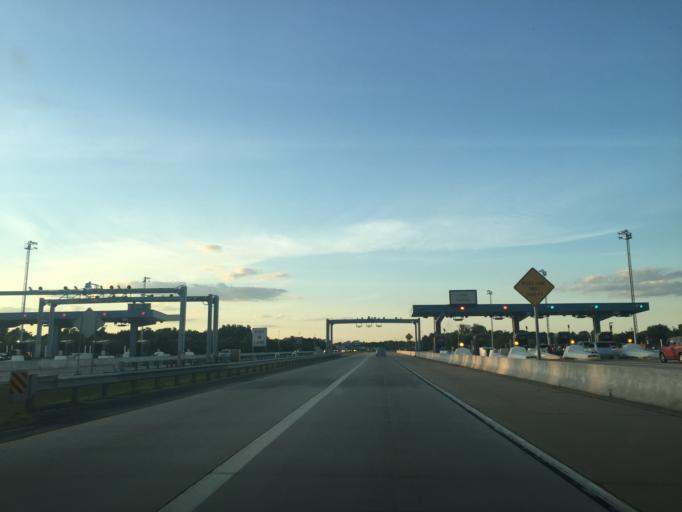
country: US
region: Delaware
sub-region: New Castle County
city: Delaware City
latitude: 39.5247
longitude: -75.6508
